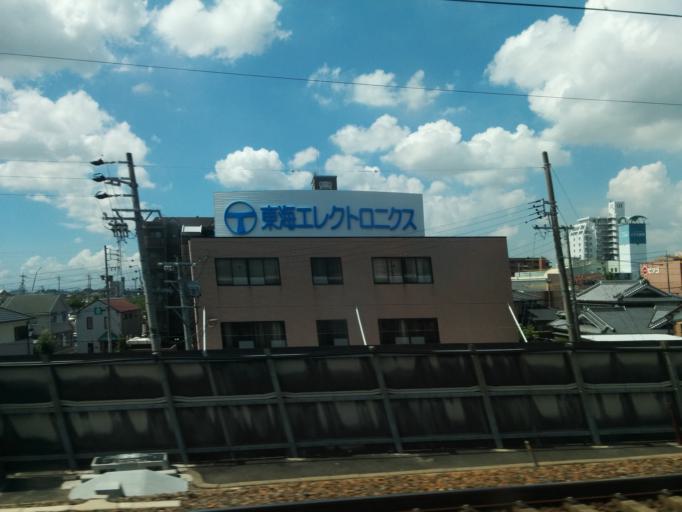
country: JP
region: Aichi
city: Anjo
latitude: 34.9650
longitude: 137.0641
